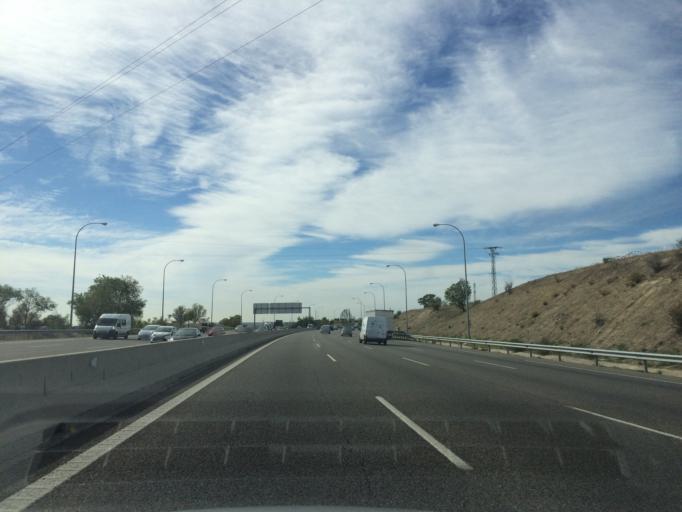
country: ES
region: Madrid
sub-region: Provincia de Madrid
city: Fuencarral-El Pardo
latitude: 40.4967
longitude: -3.7261
